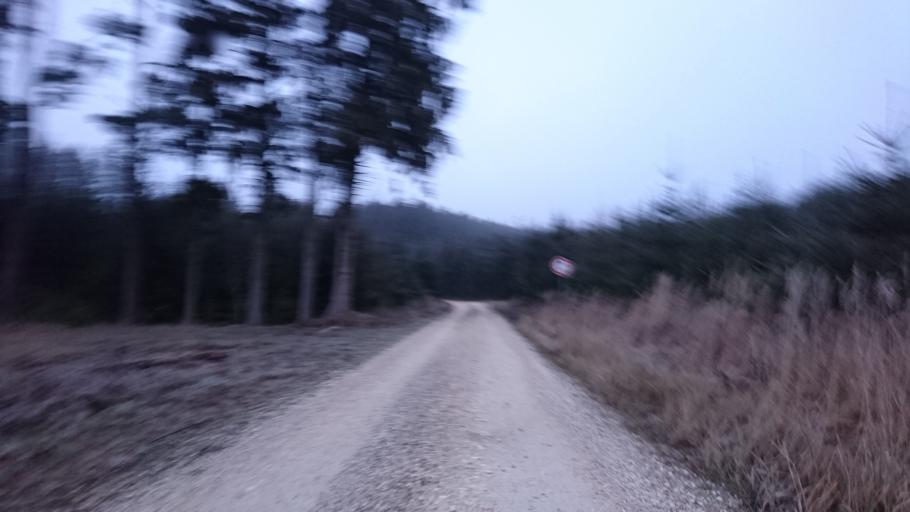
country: DE
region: Bavaria
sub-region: Swabia
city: Altenmunster
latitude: 48.4375
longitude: 10.6209
